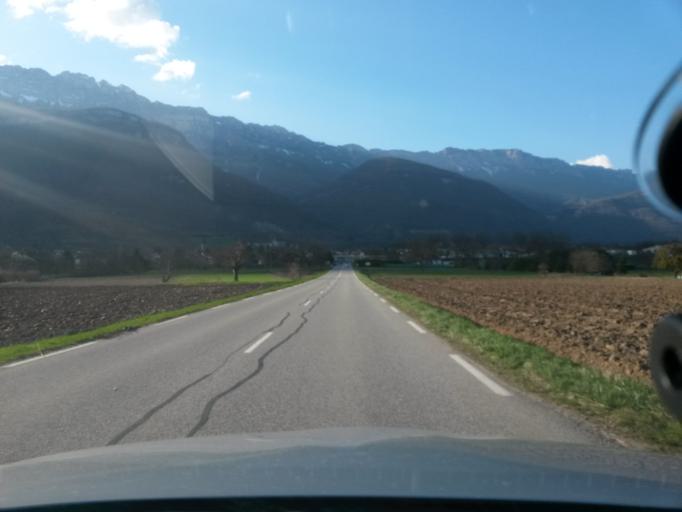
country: FR
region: Rhone-Alpes
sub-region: Departement de l'Isere
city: Le Touvet
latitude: 45.3543
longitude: 5.9597
